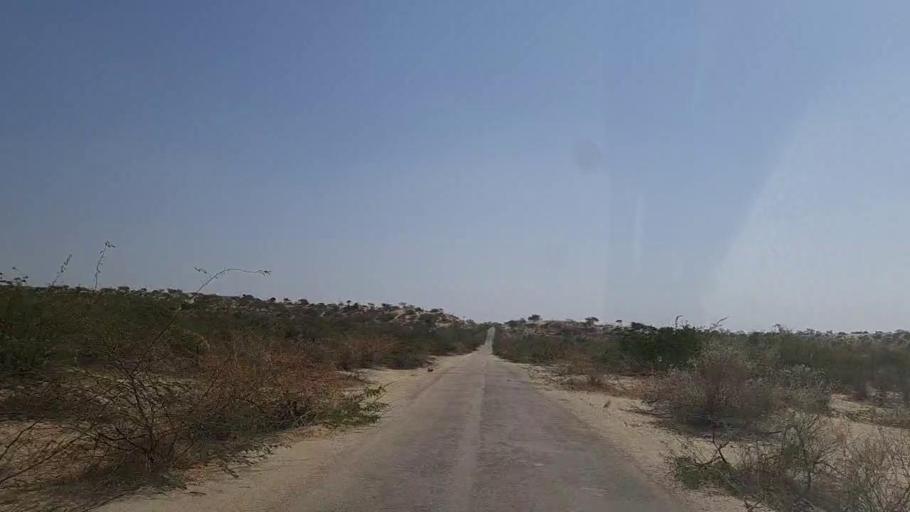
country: PK
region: Sindh
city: Diplo
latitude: 24.4926
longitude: 69.4358
